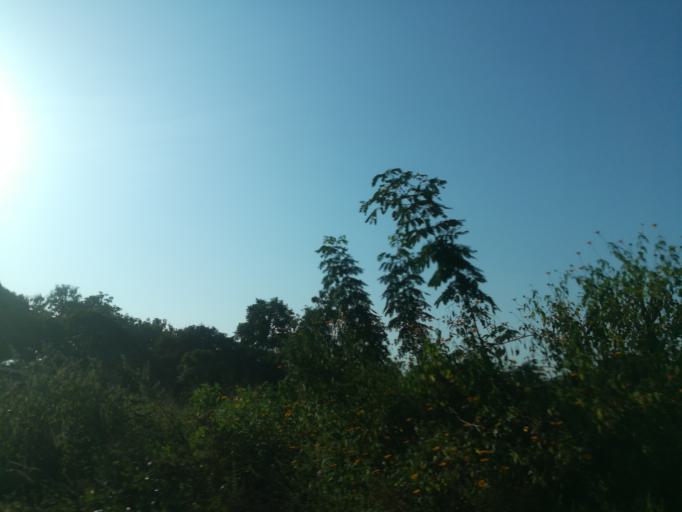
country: NG
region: Ogun
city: Abeokuta
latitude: 7.2027
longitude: 3.2894
